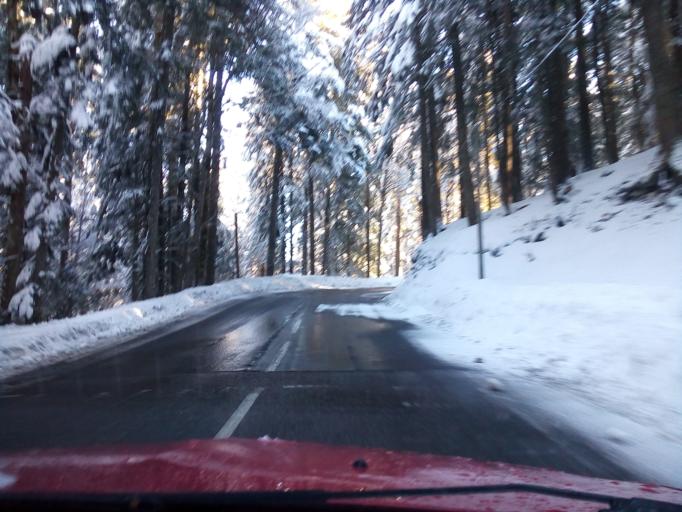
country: FR
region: Rhone-Alpes
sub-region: Departement de l'Isere
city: Le Sappey-en-Chartreuse
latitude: 45.3019
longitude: 5.7700
